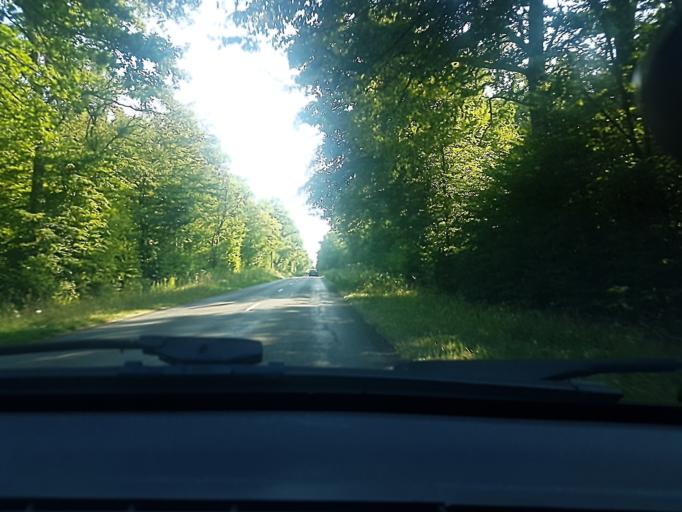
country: FR
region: Bourgogne
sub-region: Departement de Saone-et-Loire
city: Varennes-le-Grand
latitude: 46.6868
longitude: 4.8341
